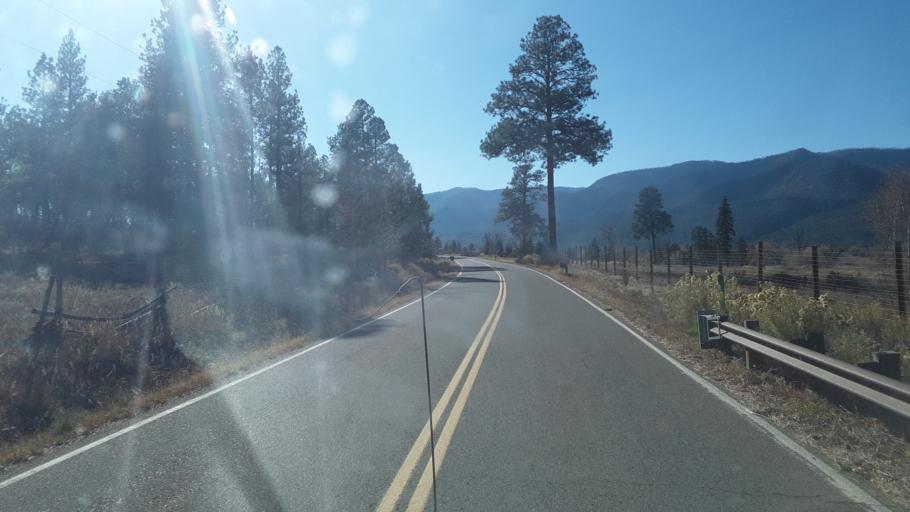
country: US
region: Colorado
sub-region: La Plata County
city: Durango
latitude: 37.4142
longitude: -107.8074
